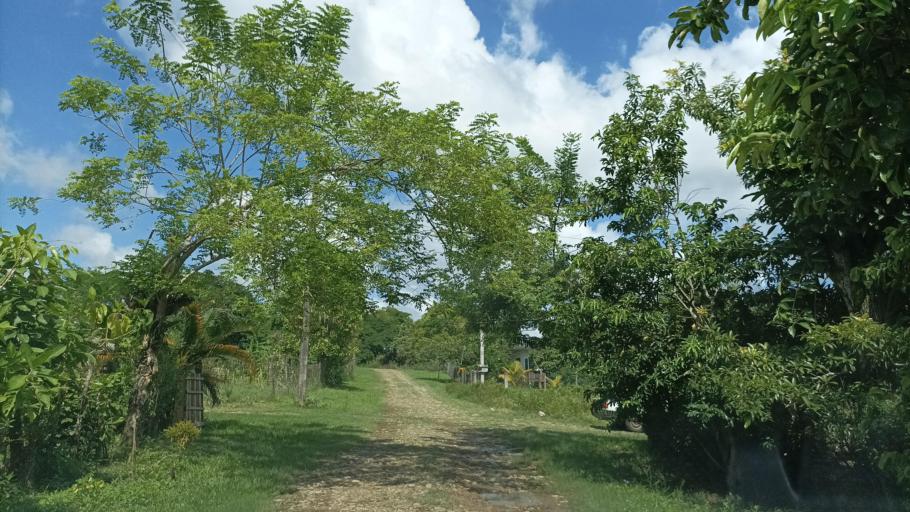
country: MX
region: Veracruz
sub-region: Tantoyuca
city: El Lindero
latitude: 21.1911
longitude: -98.1475
